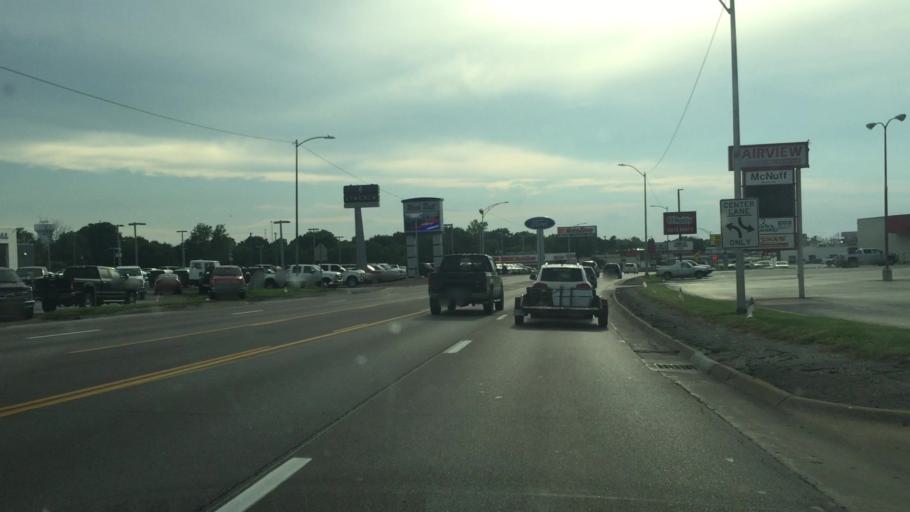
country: US
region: Missouri
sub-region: Pettis County
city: Sedalia
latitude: 38.7054
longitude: -93.2554
